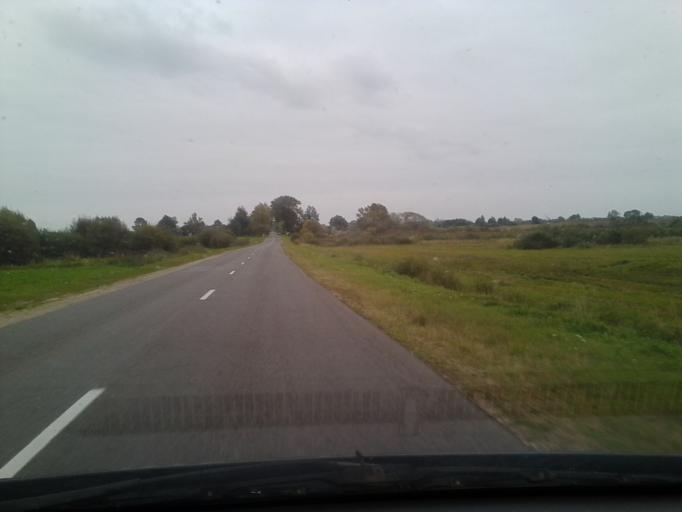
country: BY
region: Vitebsk
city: Pastavy
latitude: 55.1385
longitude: 26.9490
